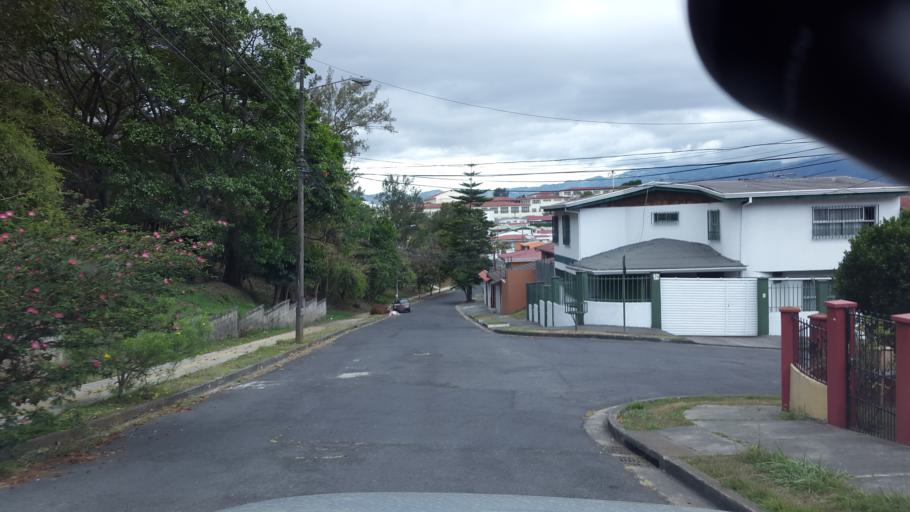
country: CR
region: San Jose
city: San Vicente de Moravia
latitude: 9.9609
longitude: -84.0558
